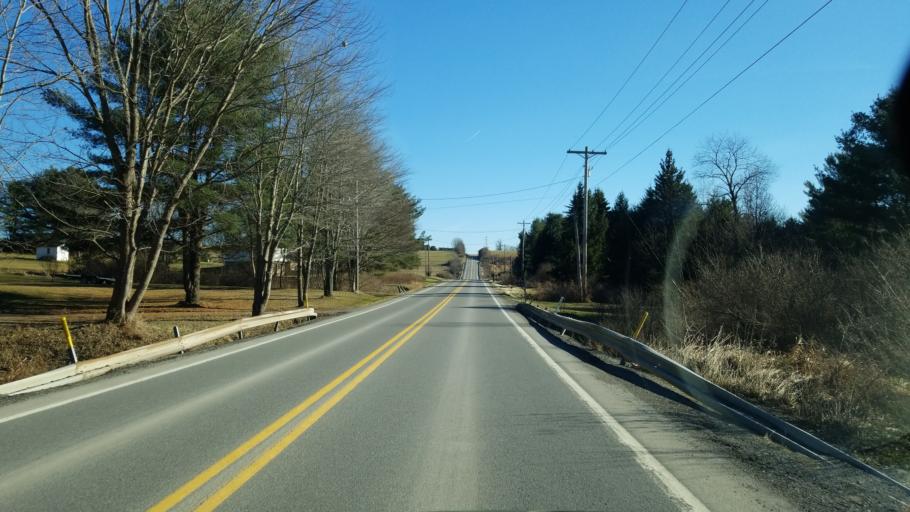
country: US
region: Pennsylvania
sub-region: Jefferson County
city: Falls Creek
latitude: 41.1820
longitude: -78.8716
